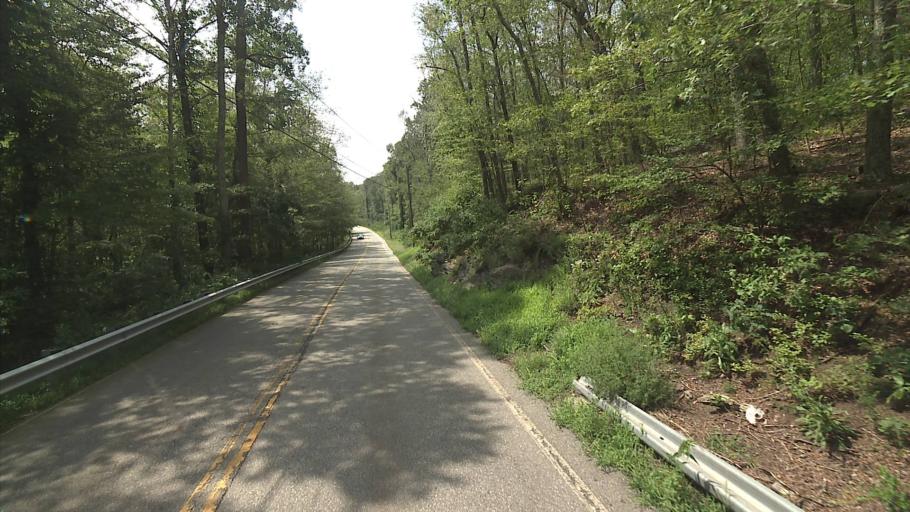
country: US
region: Connecticut
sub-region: New London County
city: Colchester
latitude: 41.4529
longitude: -72.3129
